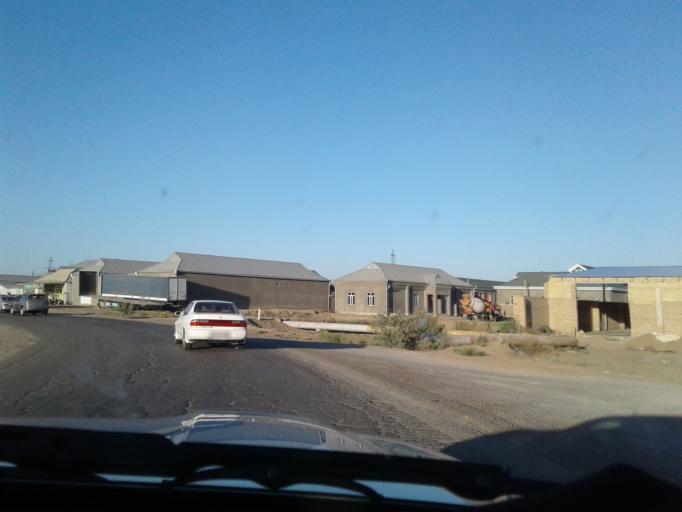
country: TM
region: Mary
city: Mary
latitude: 37.5636
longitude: 61.8245
